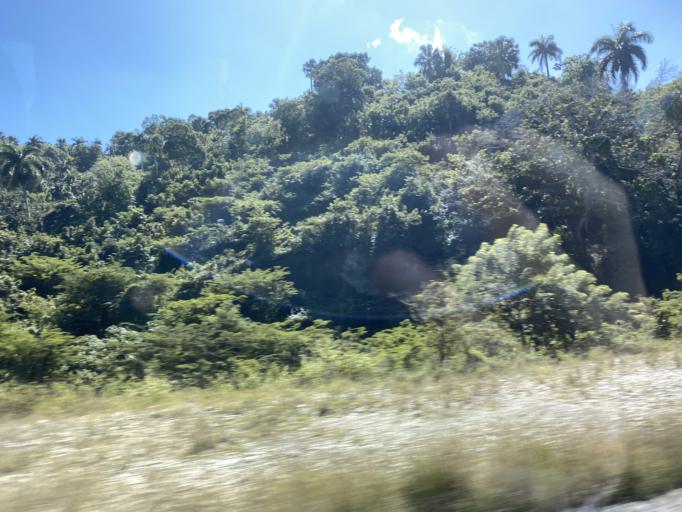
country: DO
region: Puerto Plata
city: Imbert
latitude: 19.8255
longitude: -70.7737
